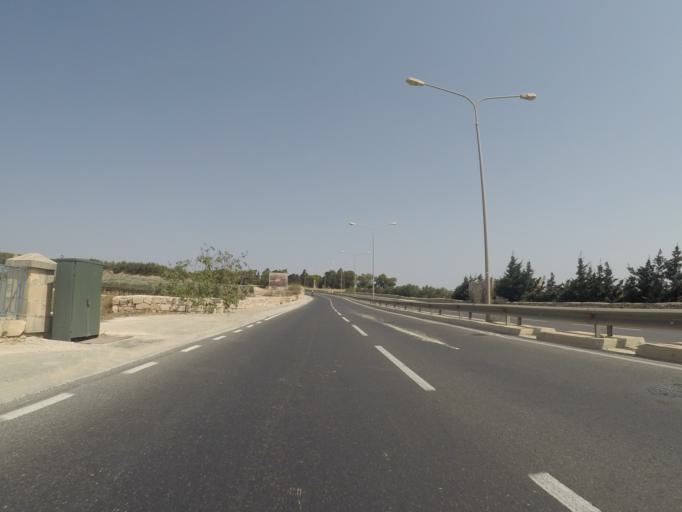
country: MT
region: L-Imdina
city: Imdina
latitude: 35.8883
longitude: 14.4100
